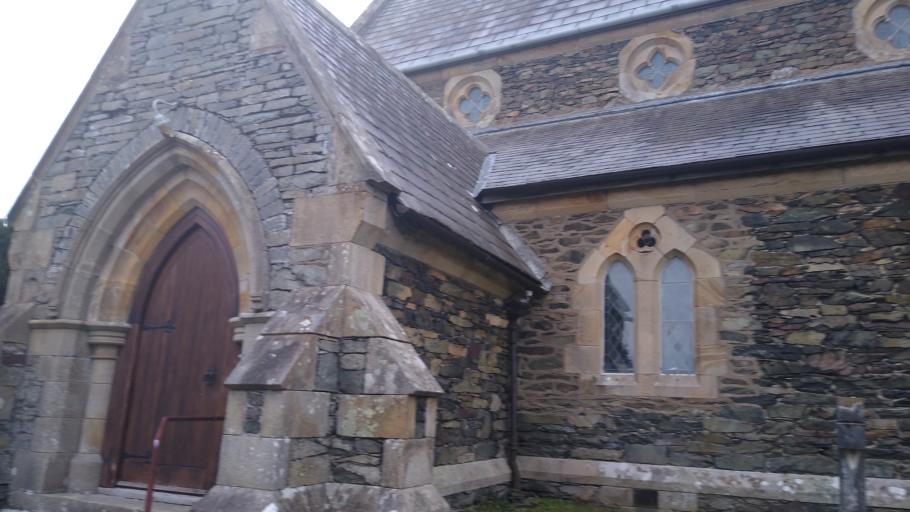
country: GB
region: England
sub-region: Cumbria
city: Millom
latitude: 54.2586
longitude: -3.2634
